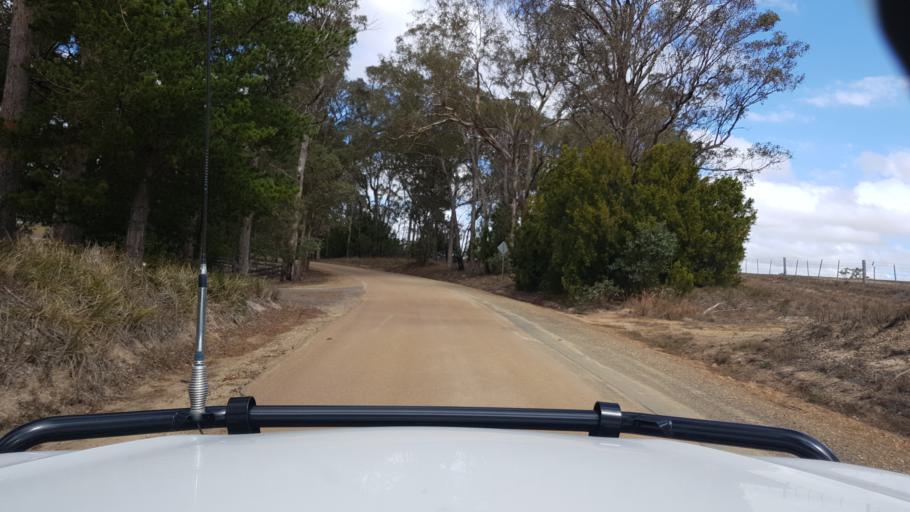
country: AU
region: Victoria
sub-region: East Gippsland
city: Bairnsdale
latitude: -37.7625
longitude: 147.6069
